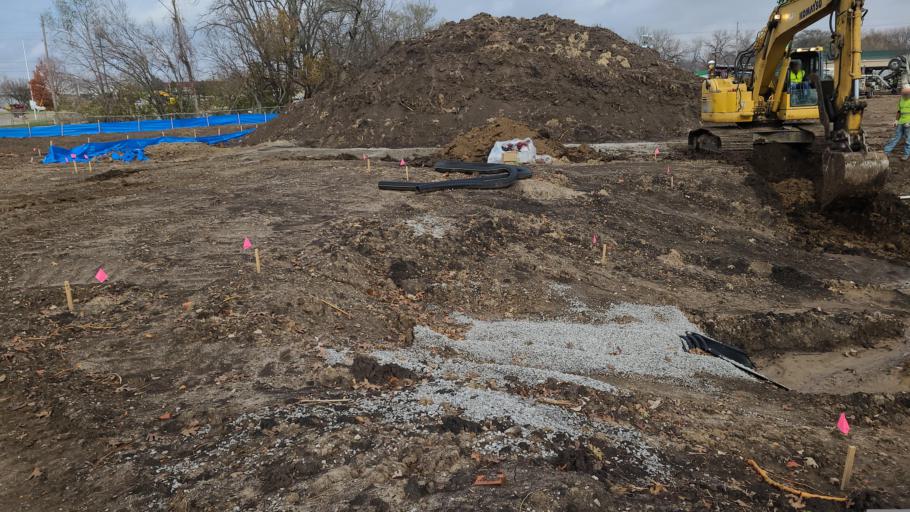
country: US
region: Kansas
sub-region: Douglas County
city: Lawrence
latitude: 38.9414
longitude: -95.2136
